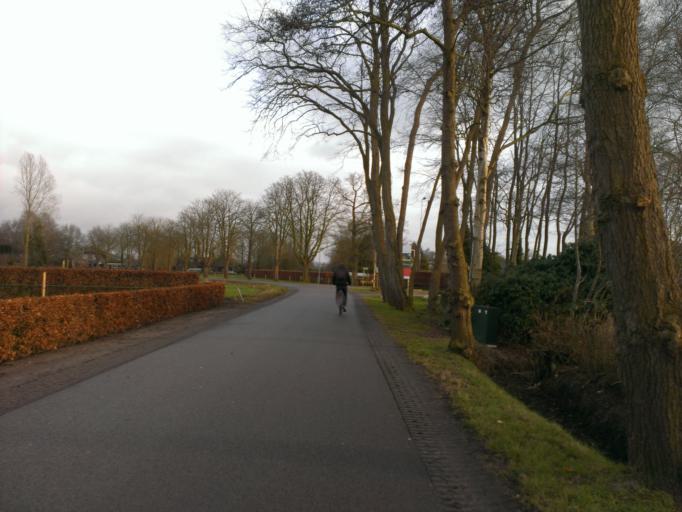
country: NL
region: Gelderland
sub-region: Gemeente Heerde
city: Heerde
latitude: 52.3748
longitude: 6.0282
